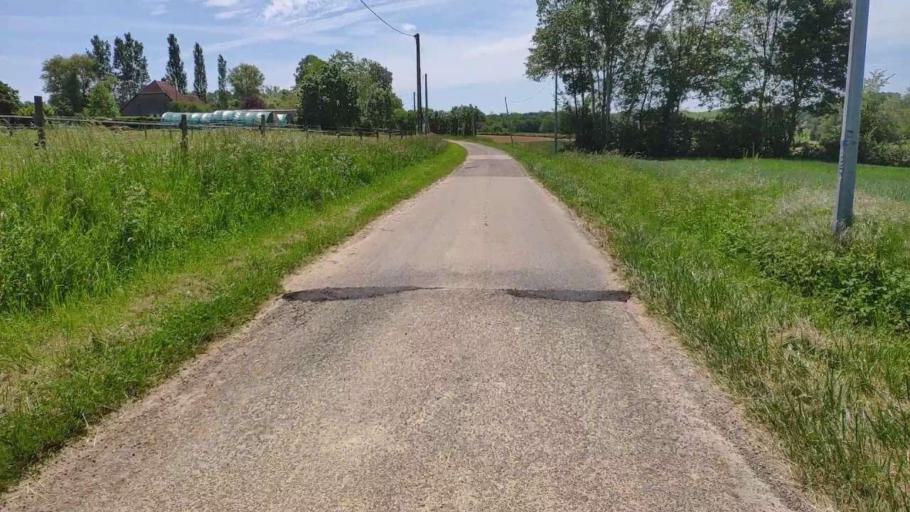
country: FR
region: Franche-Comte
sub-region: Departement du Jura
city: Bletterans
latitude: 46.7914
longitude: 5.3695
